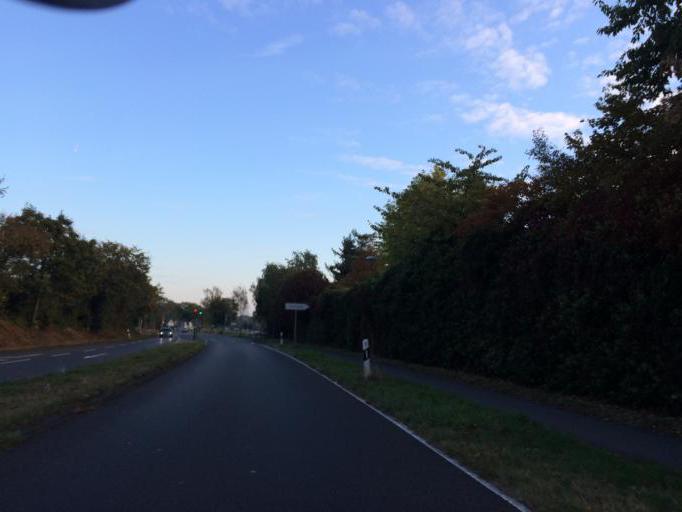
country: DE
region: North Rhine-Westphalia
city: Sankt Augustin
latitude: 50.7606
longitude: 7.1742
